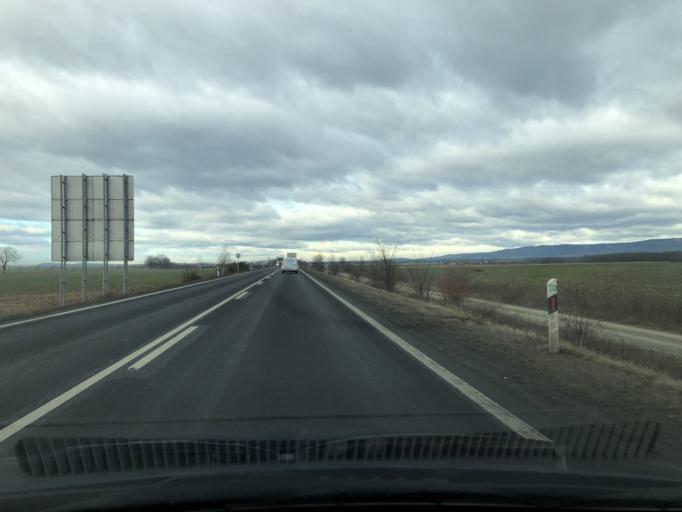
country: HU
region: Vas
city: Gencsapati
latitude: 47.2490
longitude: 16.5621
